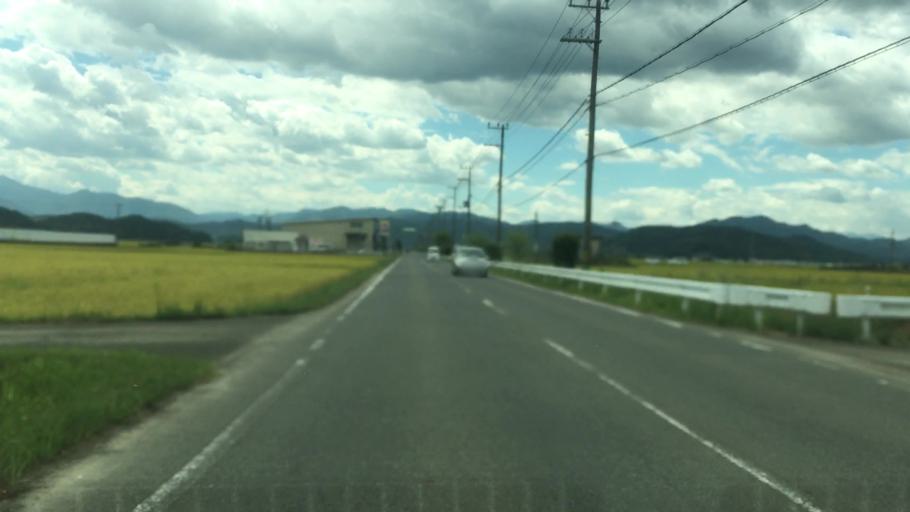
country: JP
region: Hyogo
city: Toyooka
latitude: 35.5268
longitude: 134.8398
